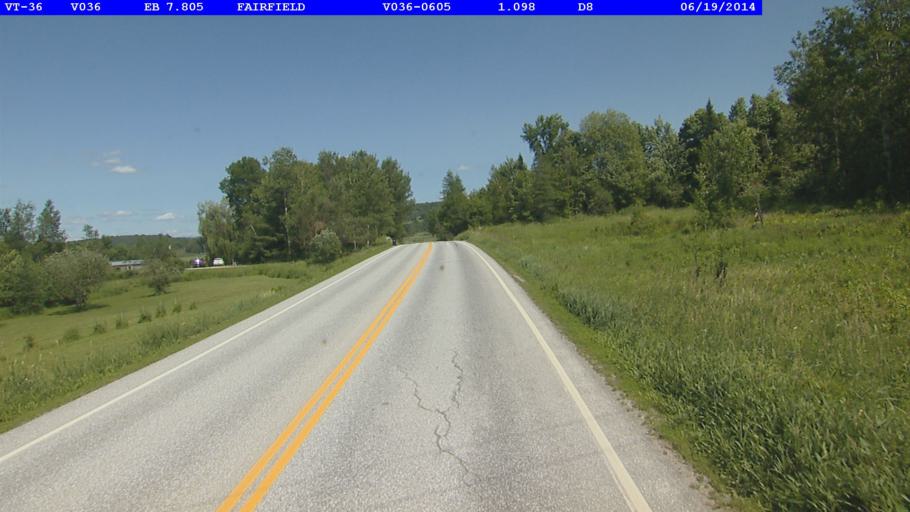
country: US
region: Vermont
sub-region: Franklin County
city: Saint Albans
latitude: 44.7875
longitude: -73.0098
